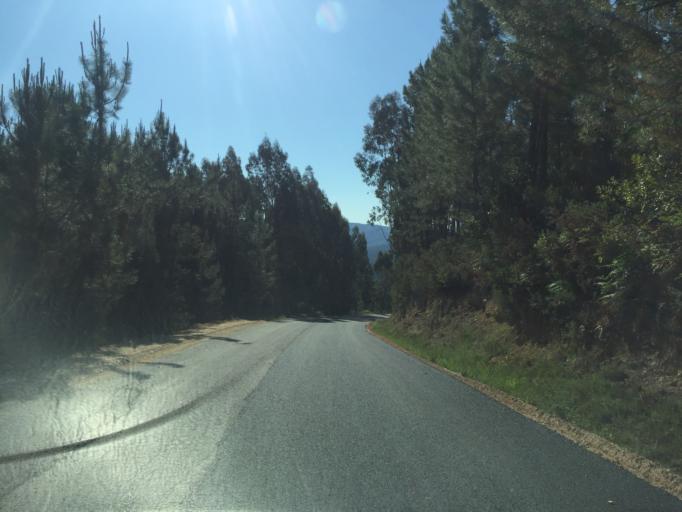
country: PT
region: Coimbra
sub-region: Pampilhosa da Serra
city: Pampilhosa da Serra
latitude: 40.0543
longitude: -7.8236
